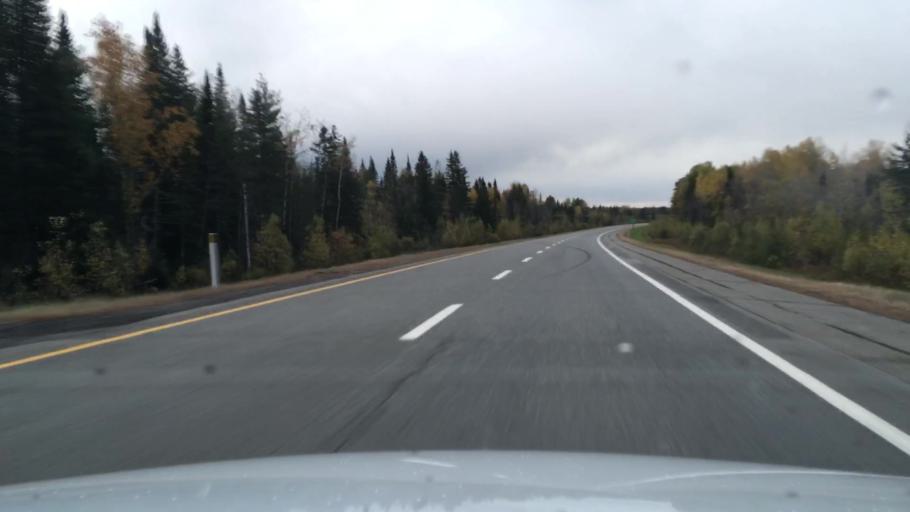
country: US
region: Maine
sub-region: Penobscot County
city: Greenbush
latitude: 45.1221
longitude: -68.6953
